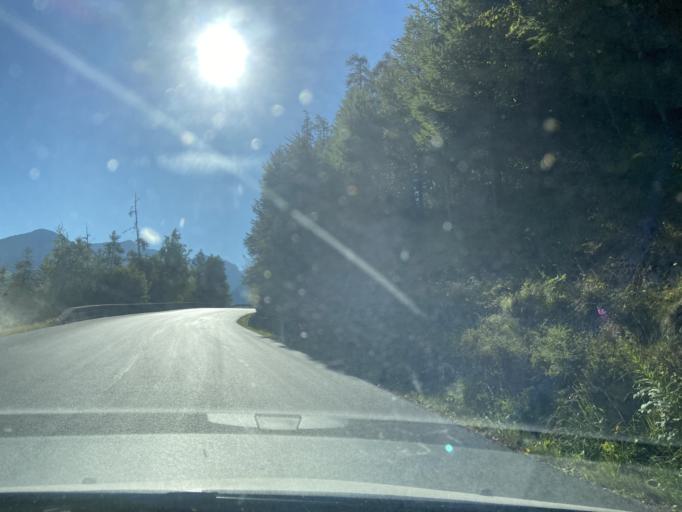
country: FR
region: Provence-Alpes-Cote d'Azur
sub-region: Departement des Hautes-Alpes
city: Guillestre
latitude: 44.6409
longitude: 6.6251
